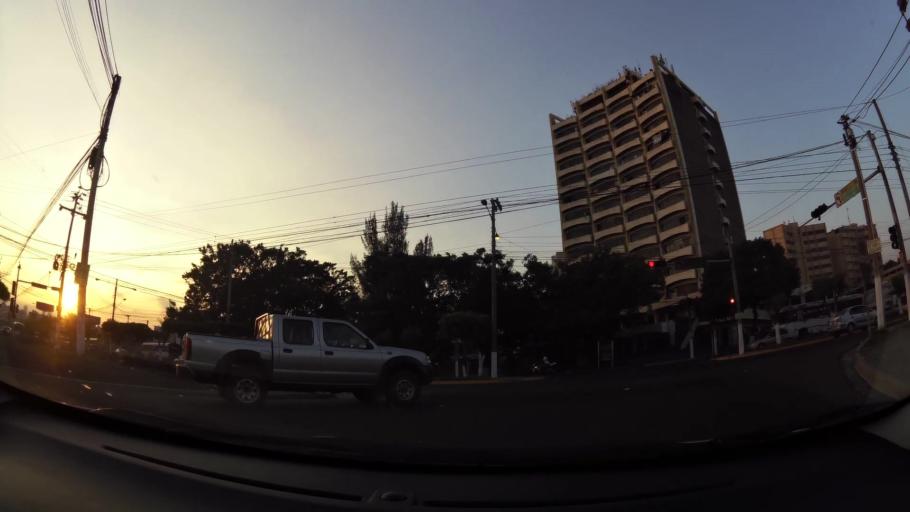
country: SV
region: San Salvador
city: San Salvador
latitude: 13.7111
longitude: -89.2070
